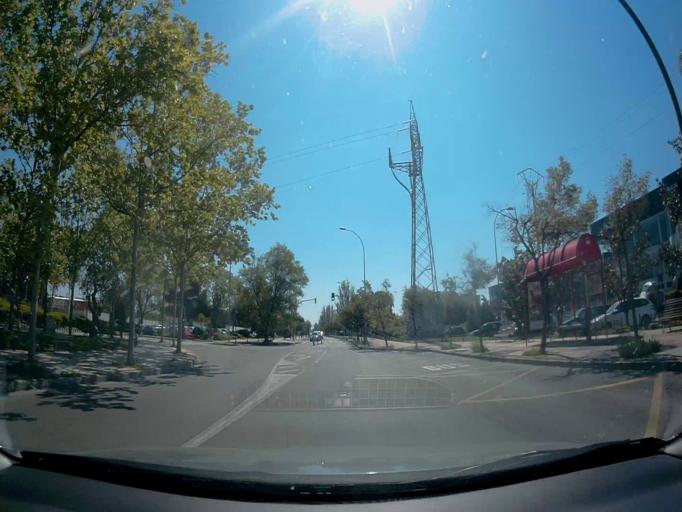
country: ES
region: Madrid
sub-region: Provincia de Madrid
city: Alcorcon
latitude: 40.3439
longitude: -3.8090
